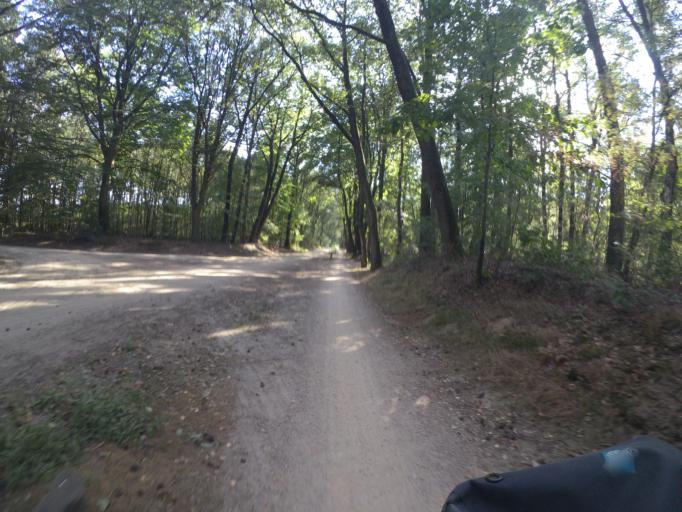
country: NL
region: Overijssel
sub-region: Gemeente Hof van Twente
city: Markelo
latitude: 52.2680
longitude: 6.5139
